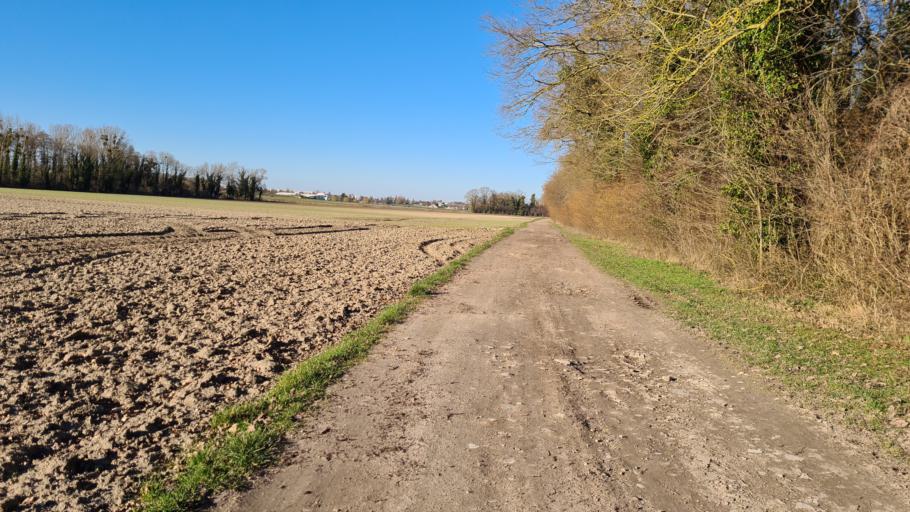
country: FR
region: Picardie
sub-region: Departement de l'Aisne
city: Bruyeres-et-Montberault
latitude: 49.5561
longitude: 3.6557
